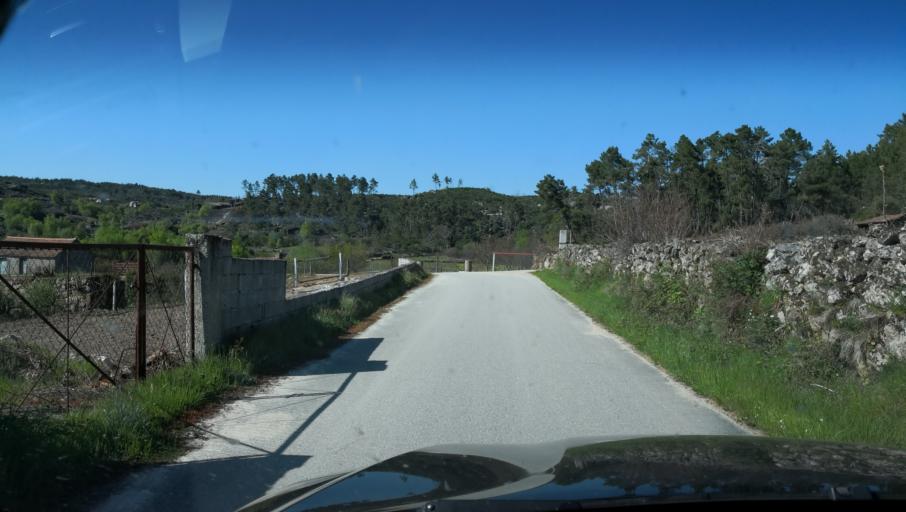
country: PT
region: Vila Real
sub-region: Sabrosa
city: Sabrosa
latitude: 41.2992
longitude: -7.6403
